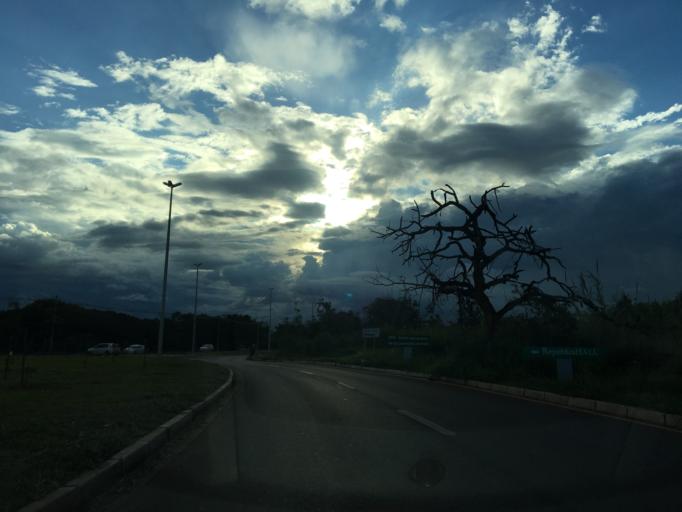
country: BR
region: Federal District
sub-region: Brasilia
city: Brasilia
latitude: -15.8137
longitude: -47.8486
